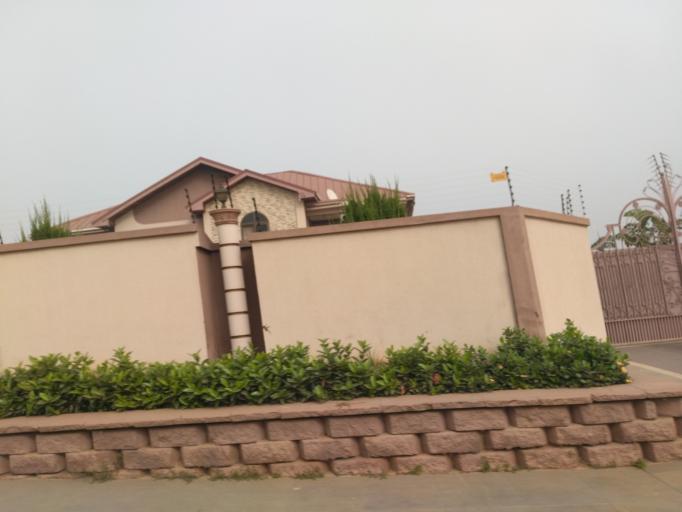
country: GH
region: Ashanti
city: Kumasi
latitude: 6.6536
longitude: -1.6279
